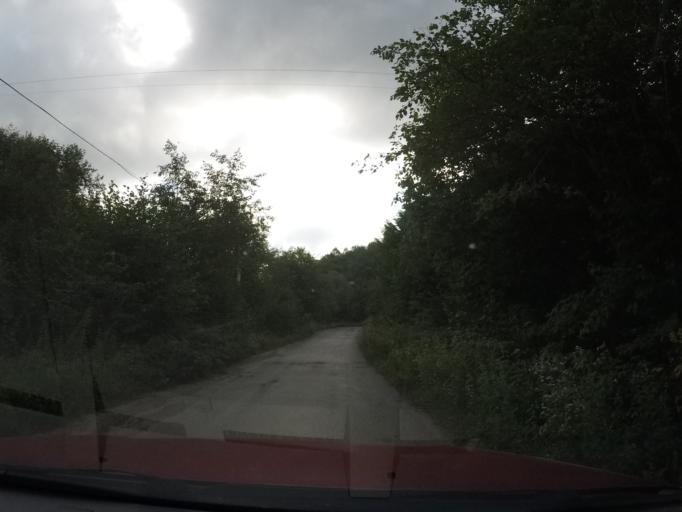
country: UA
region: Zakarpattia
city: Velykyi Bereznyi
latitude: 48.9513
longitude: 22.6650
